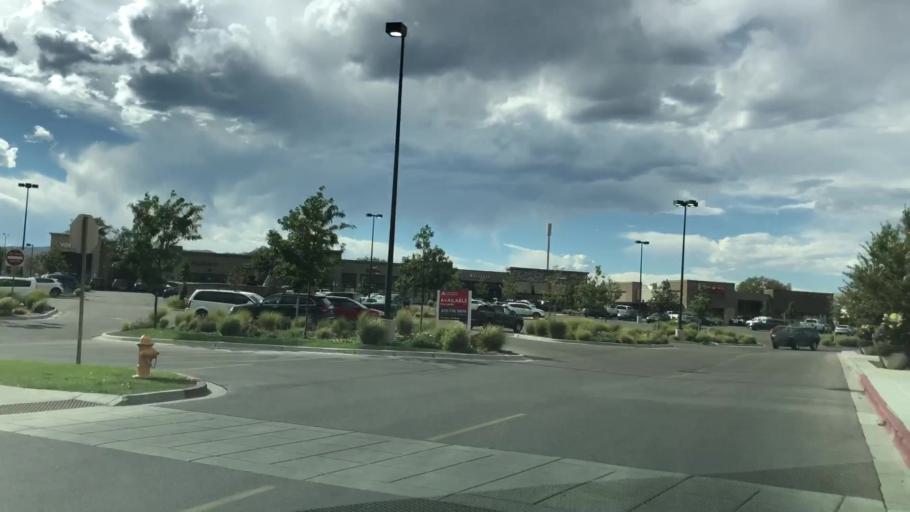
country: US
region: Colorado
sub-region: Larimer County
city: Fort Collins
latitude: 40.5414
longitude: -105.0748
